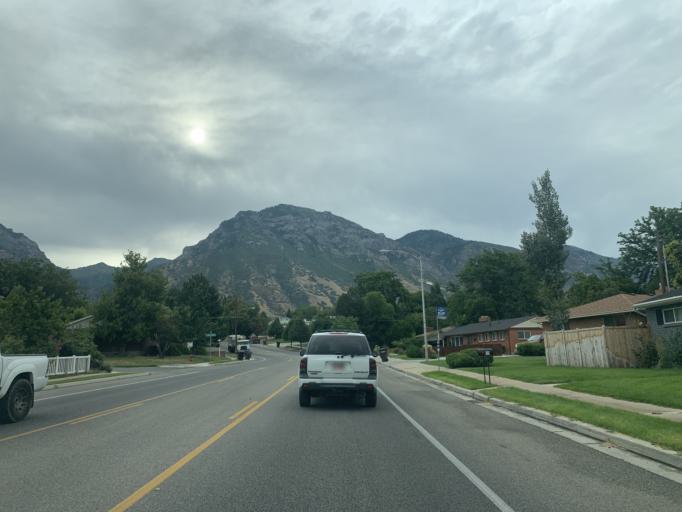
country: US
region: Utah
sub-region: Utah County
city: Provo
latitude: 40.2632
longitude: -111.6534
